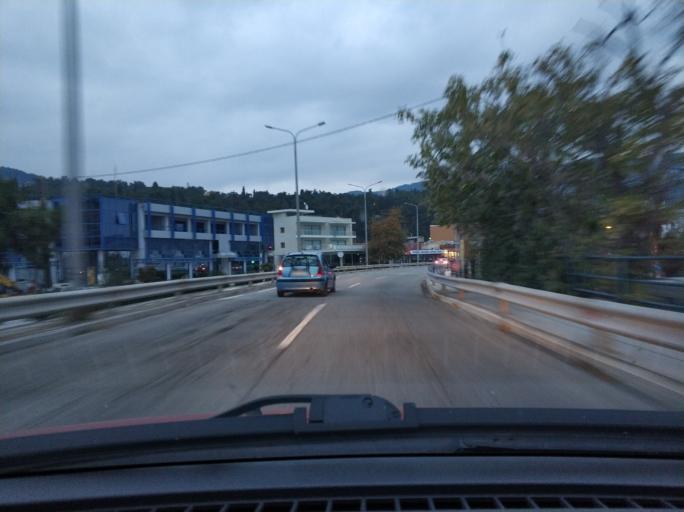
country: GR
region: East Macedonia and Thrace
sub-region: Nomos Kavalas
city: Kavala
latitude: 40.9275
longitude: 24.3909
